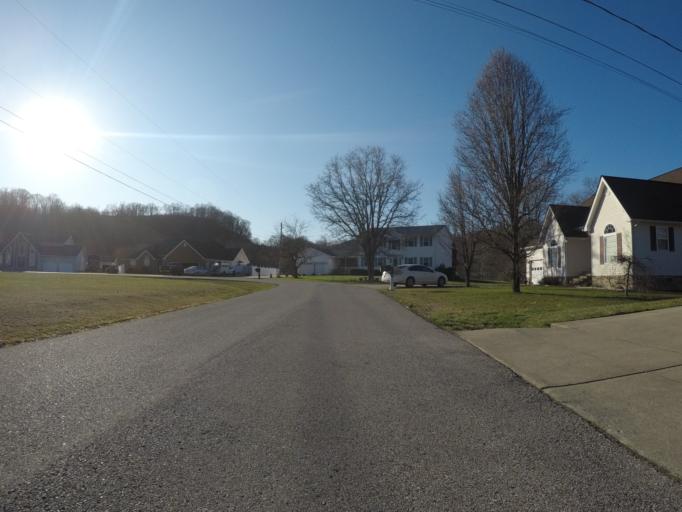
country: US
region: West Virginia
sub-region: Cabell County
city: Huntington
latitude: 38.4606
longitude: -82.4398
